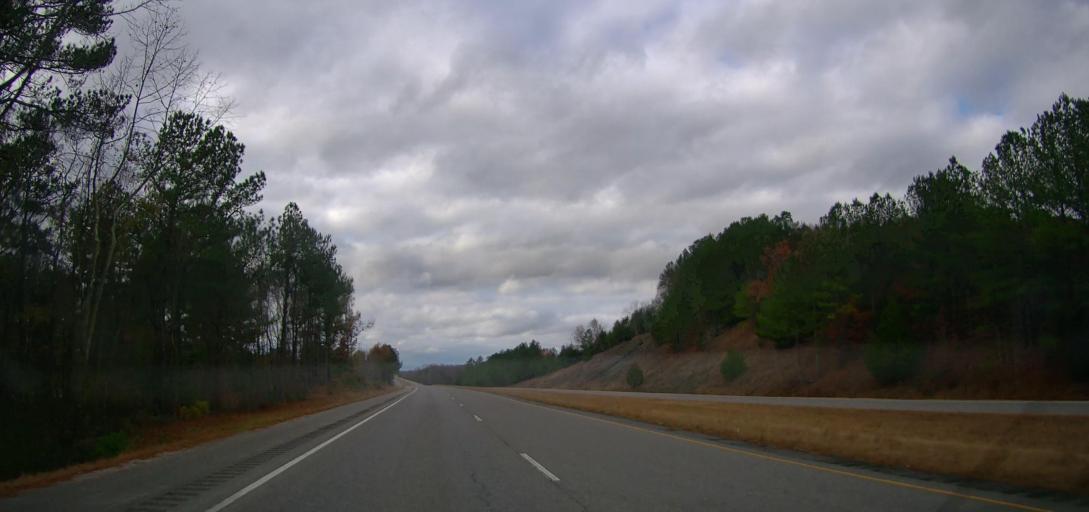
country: US
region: Alabama
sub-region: Lawrence County
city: Town Creek
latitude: 34.6264
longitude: -87.4768
